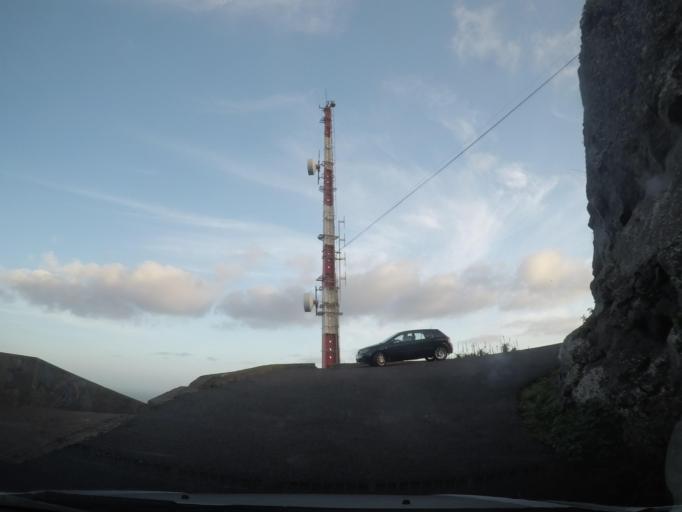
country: PT
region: Madeira
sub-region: Machico
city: Canical
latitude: 32.7241
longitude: -16.7586
